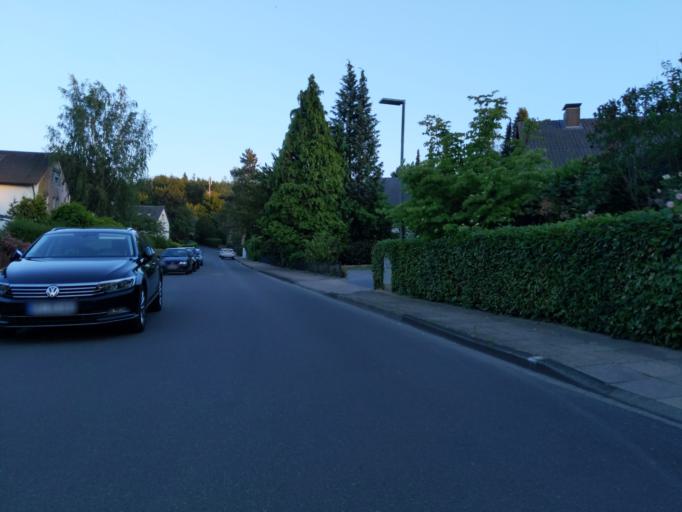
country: DE
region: North Rhine-Westphalia
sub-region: Regierungsbezirk Detmold
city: Bielefeld
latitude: 52.0242
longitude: 8.4828
